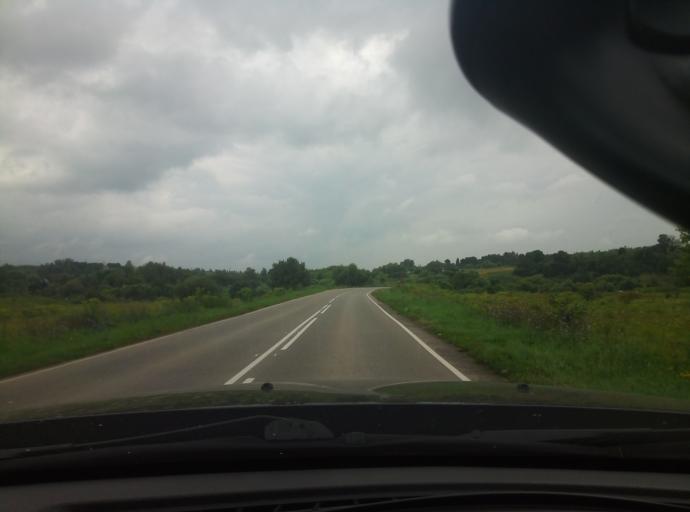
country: RU
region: Tula
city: Lomintsevskiy
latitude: 53.9609
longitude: 37.6509
